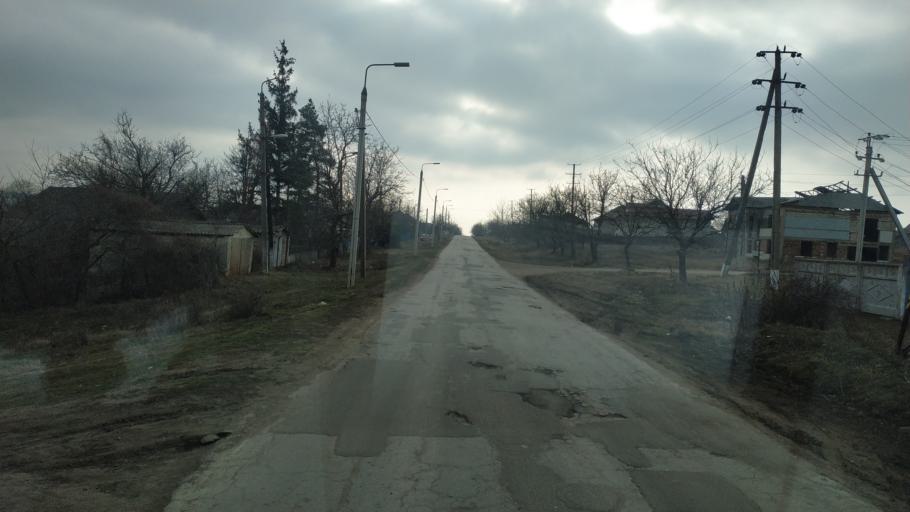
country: MD
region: Hincesti
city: Dancu
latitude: 46.8198
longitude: 28.2739
